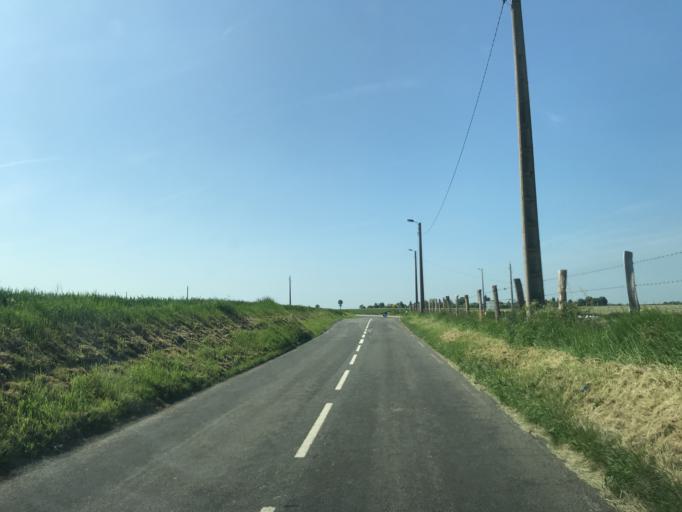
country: FR
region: Haute-Normandie
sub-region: Departement de la Seine-Maritime
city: Les Authieux-sur-le-Port-Saint-Ouen
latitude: 49.3507
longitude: 1.1466
